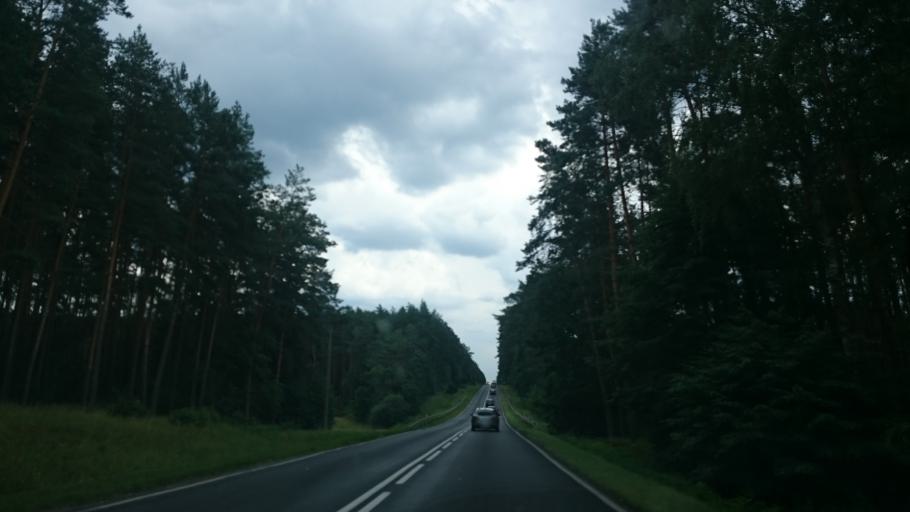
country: PL
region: Kujawsko-Pomorskie
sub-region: Powiat tucholski
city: Tuchola
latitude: 53.5503
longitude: 17.9249
